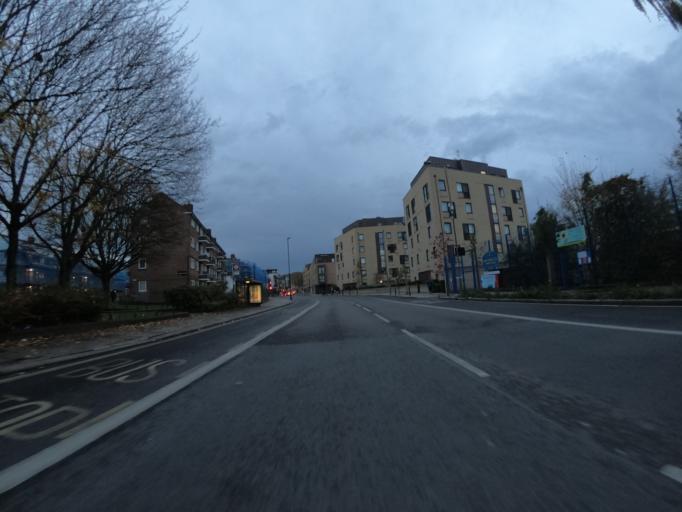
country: GB
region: England
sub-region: Greater London
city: Blackheath
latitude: 51.4880
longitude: 0.0077
